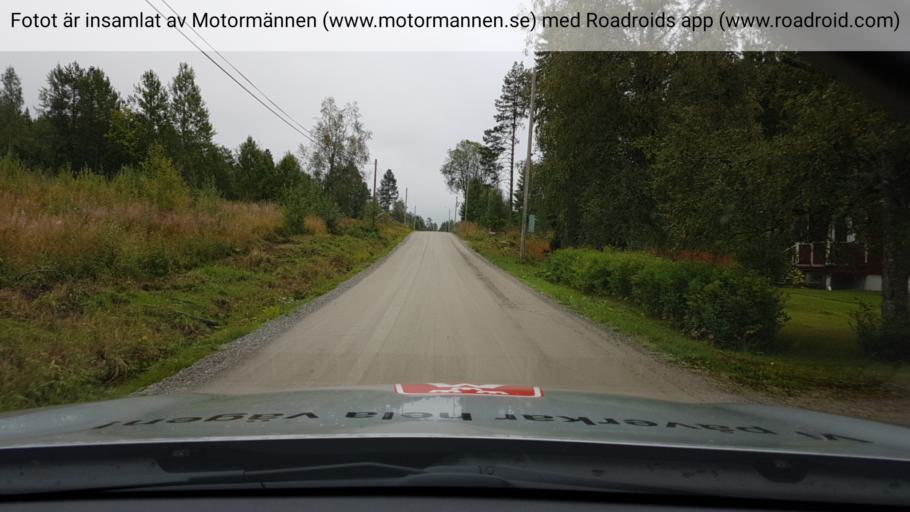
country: SE
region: Jaemtland
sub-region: Braecke Kommun
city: Braecke
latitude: 62.7732
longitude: 15.4811
